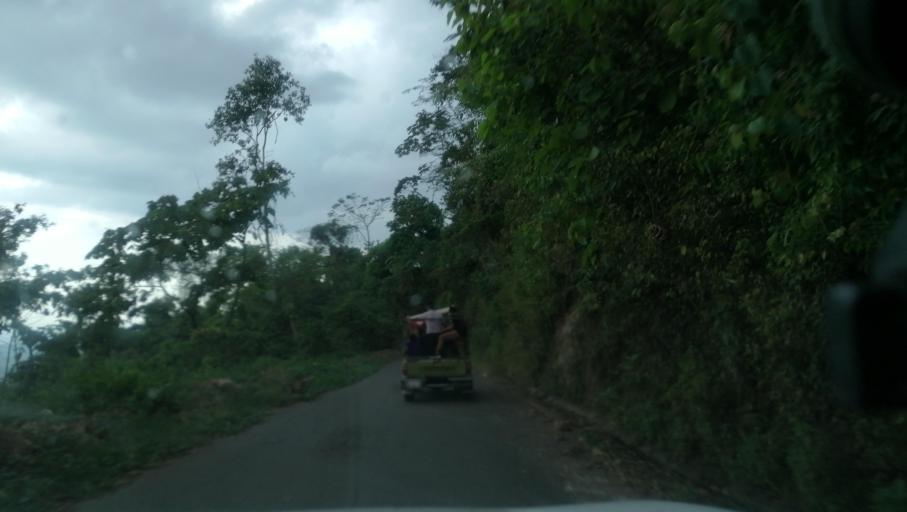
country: MX
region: Chiapas
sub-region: Cacahoatan
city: Benito Juarez
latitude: 15.0702
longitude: -92.1762
